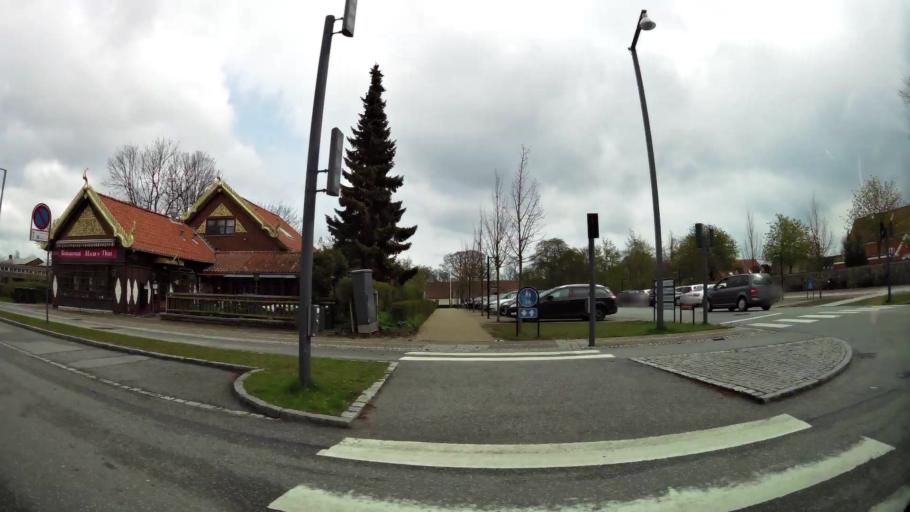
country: DK
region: Capital Region
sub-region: Rodovre Kommune
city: Rodovre
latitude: 55.6825
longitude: 12.4649
